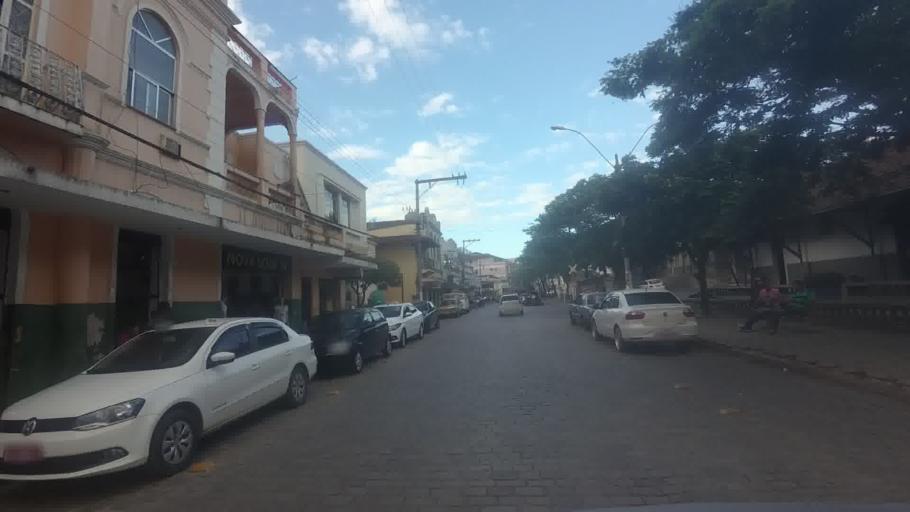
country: BR
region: Espirito Santo
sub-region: Mimoso Do Sul
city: Mimoso do Sul
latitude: -20.9522
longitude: -41.3470
